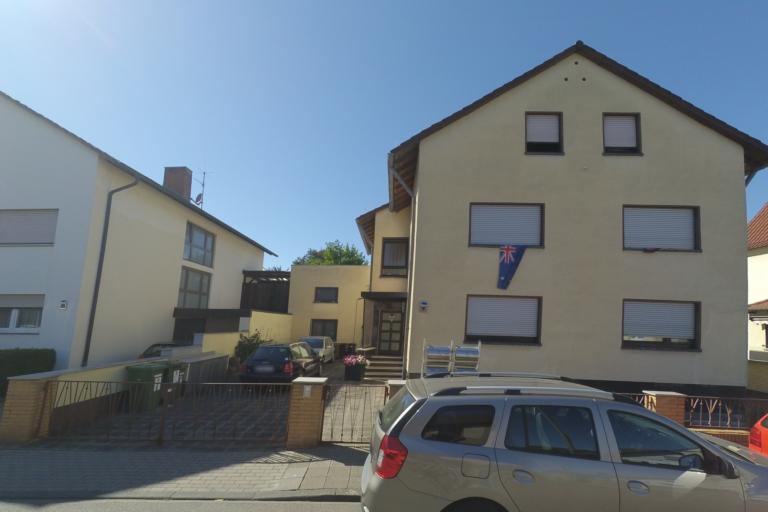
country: DE
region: Hesse
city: Viernheim
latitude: 49.5425
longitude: 8.5732
